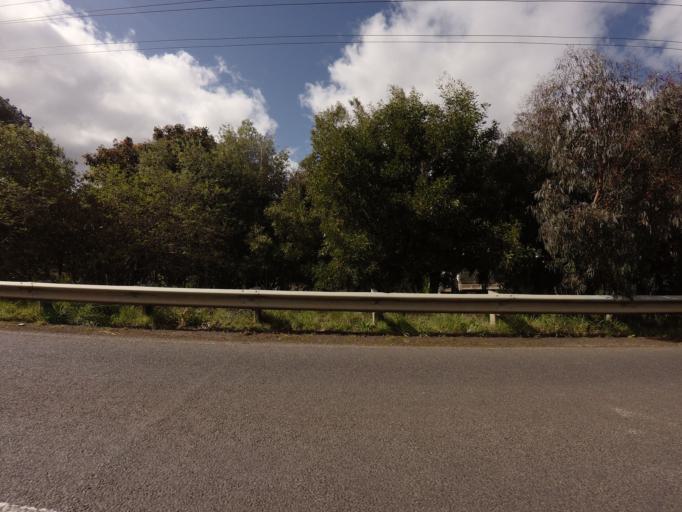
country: AU
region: Tasmania
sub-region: Huon Valley
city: Cygnet
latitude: -43.3098
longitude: 147.0131
